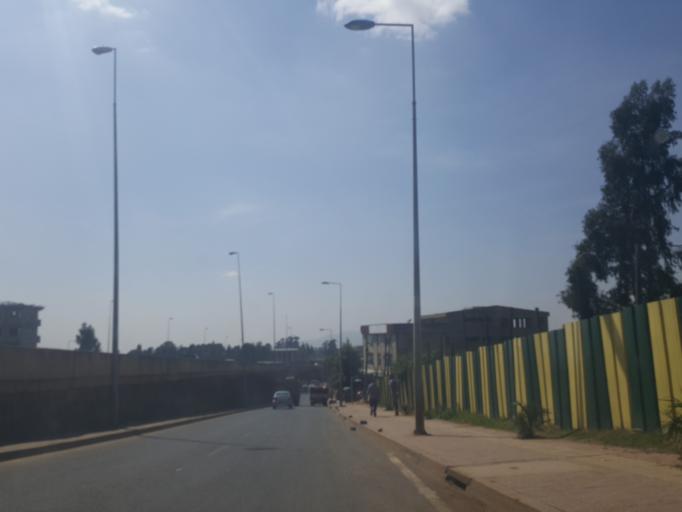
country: ET
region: Adis Abeba
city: Addis Ababa
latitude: 9.0617
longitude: 38.7144
